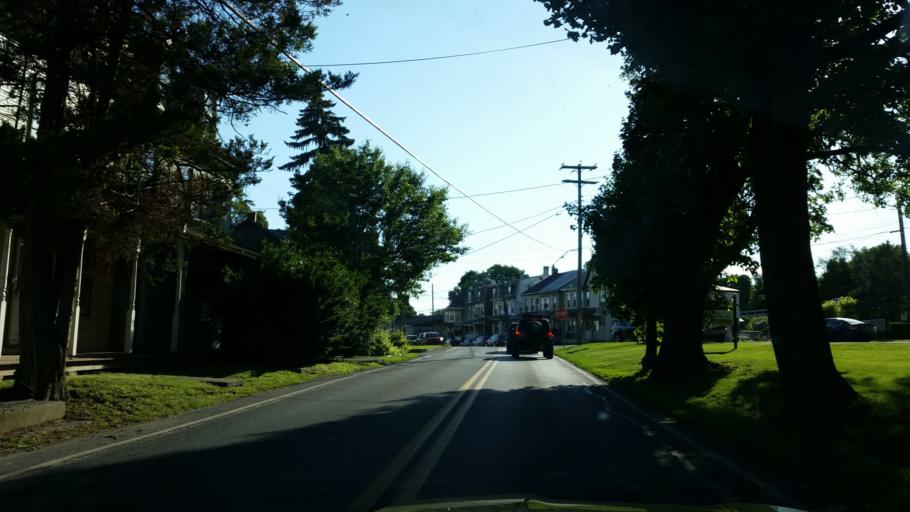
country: US
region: Pennsylvania
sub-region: Lebanon County
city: Avon
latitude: 40.3456
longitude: -76.3894
